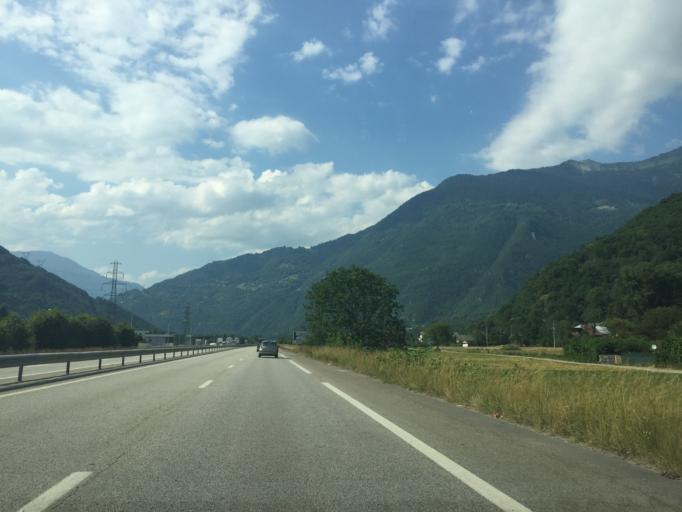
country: FR
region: Rhone-Alpes
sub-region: Departement de la Savoie
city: La Bathie
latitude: 45.6350
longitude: 6.4422
